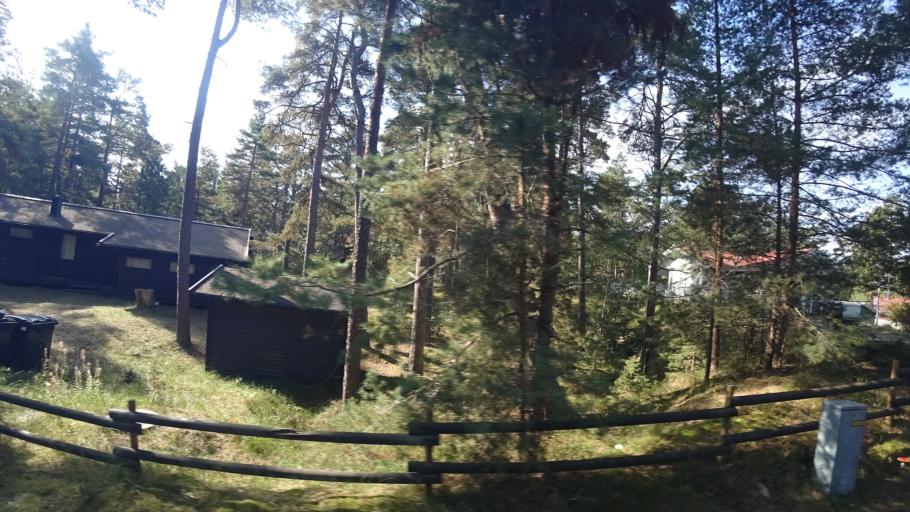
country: SE
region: Skane
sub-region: Kristianstads Kommun
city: Ahus
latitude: 55.9152
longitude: 14.3114
